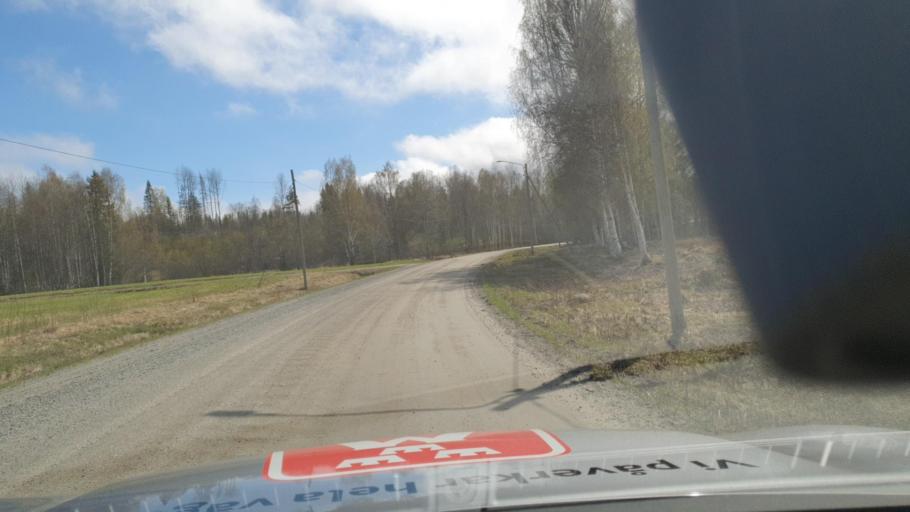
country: SE
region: Vaesterbotten
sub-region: Bjurholms Kommun
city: Bjurholm
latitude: 63.6939
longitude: 18.9574
